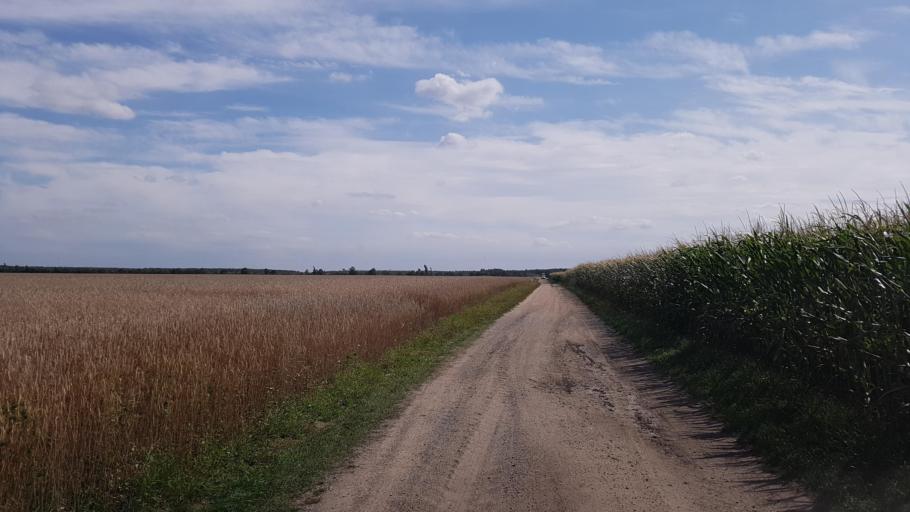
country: DE
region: Brandenburg
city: Muhlberg
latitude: 51.4636
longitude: 13.2816
